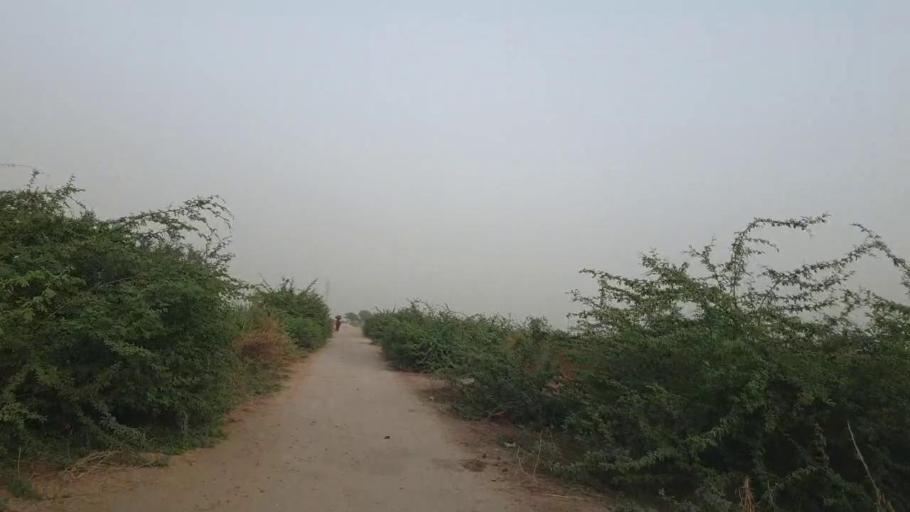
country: PK
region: Sindh
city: Kunri
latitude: 25.1078
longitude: 69.5264
